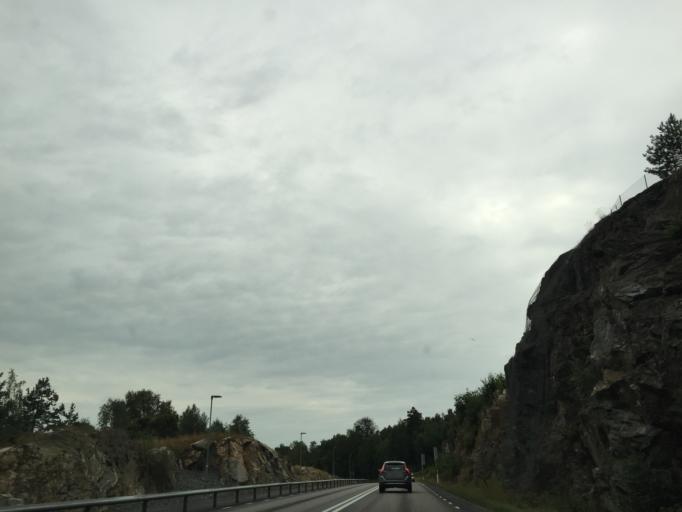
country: SE
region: Vaestra Goetaland
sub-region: Tjorns Kommun
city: Myggenas
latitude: 58.0549
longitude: 11.7583
